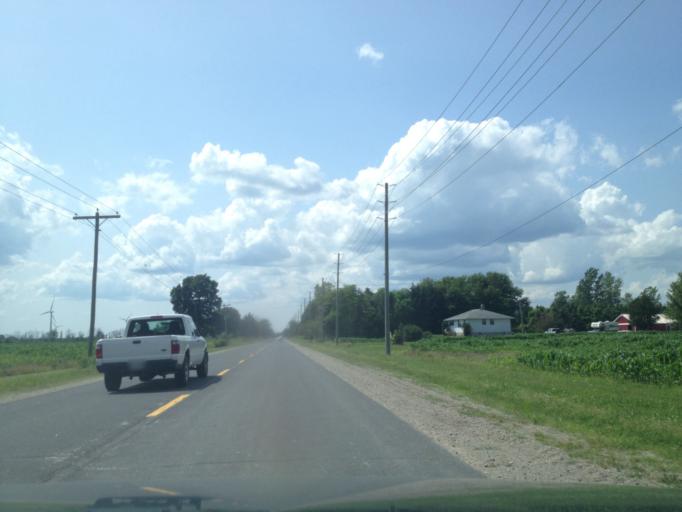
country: CA
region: Ontario
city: Aylmer
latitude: 42.6634
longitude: -80.8177
